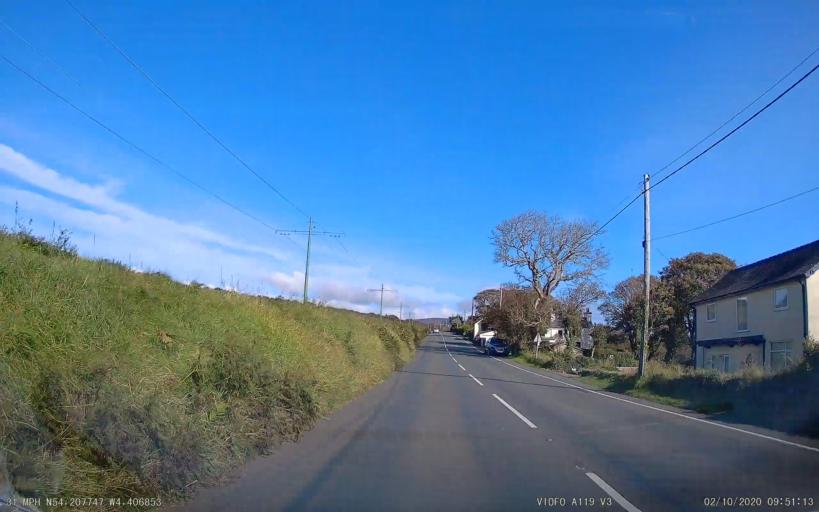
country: IM
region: Laxey
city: Laxey
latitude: 54.2077
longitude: -4.4069
